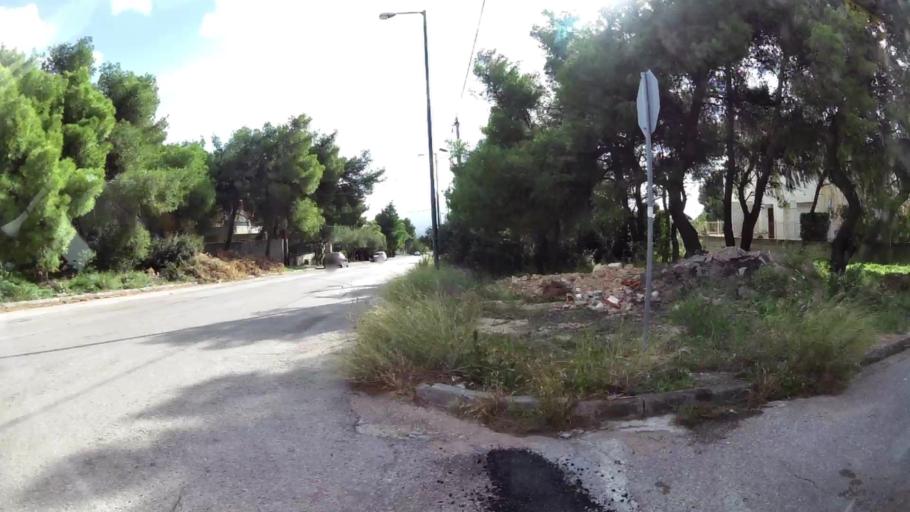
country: GR
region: Attica
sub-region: Nomarchia Anatolikis Attikis
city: Thrakomakedones
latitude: 38.1278
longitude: 23.7622
